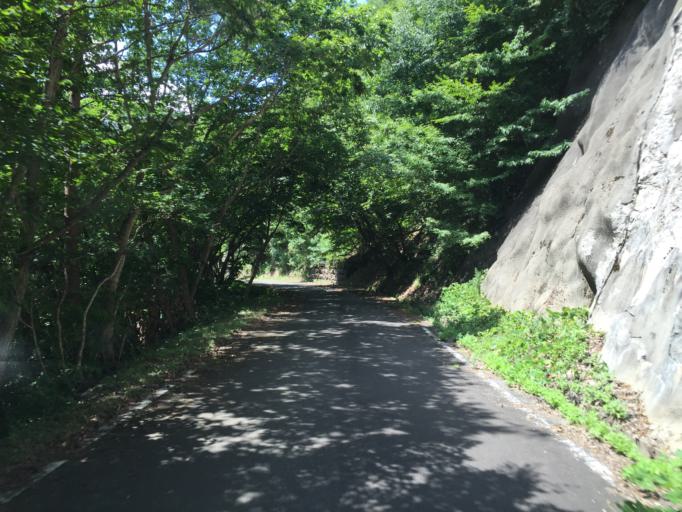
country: JP
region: Fukushima
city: Inawashiro
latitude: 37.4465
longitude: 140.0571
